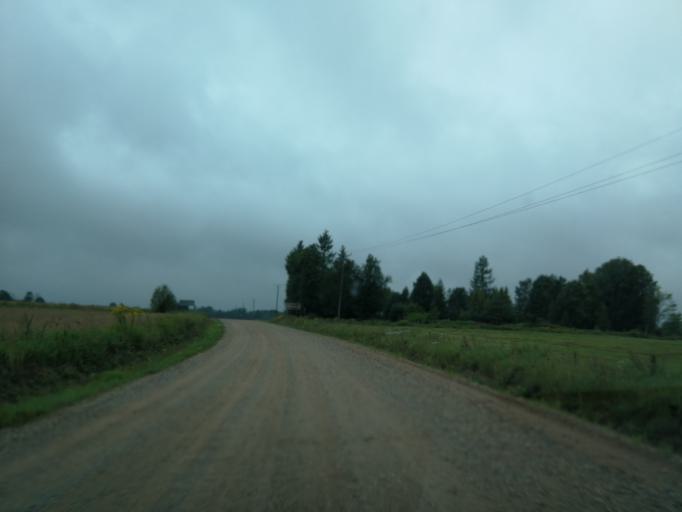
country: LV
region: Vilanu
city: Vilani
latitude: 56.3729
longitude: 27.0308
